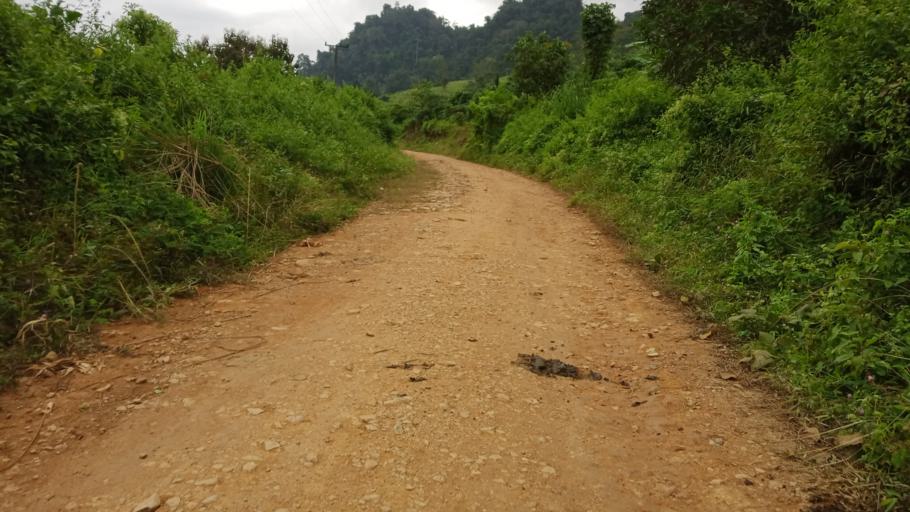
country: LA
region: Xiangkhoang
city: Phonsavan
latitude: 19.0816
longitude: 103.0123
